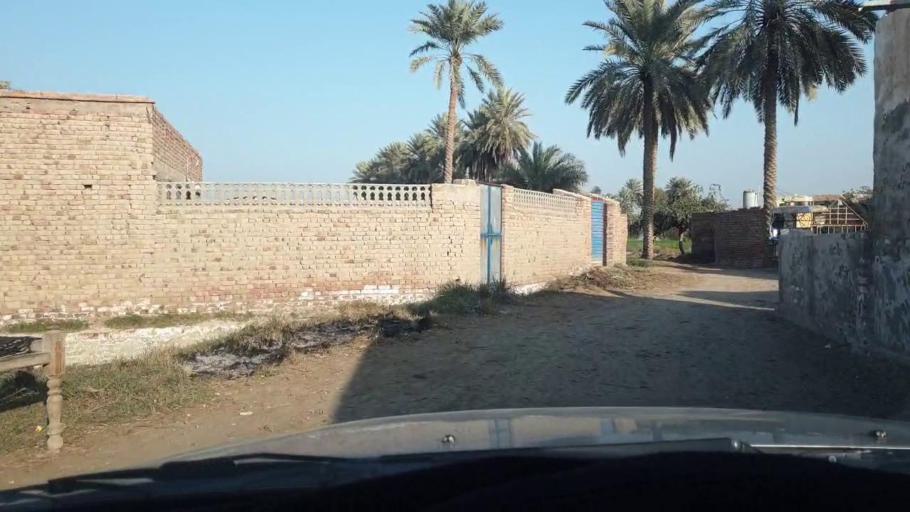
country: PK
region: Sindh
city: Mirpur Mathelo
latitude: 28.0252
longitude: 69.6043
